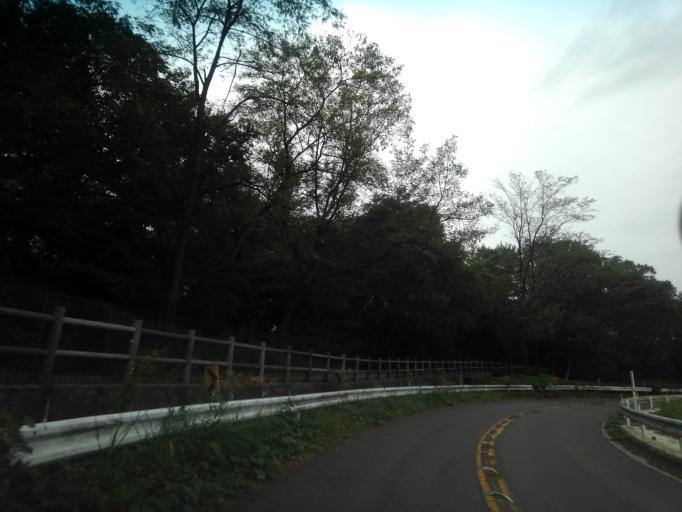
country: JP
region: Tokyo
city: Higashimurayama-shi
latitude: 35.7668
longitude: 139.4322
